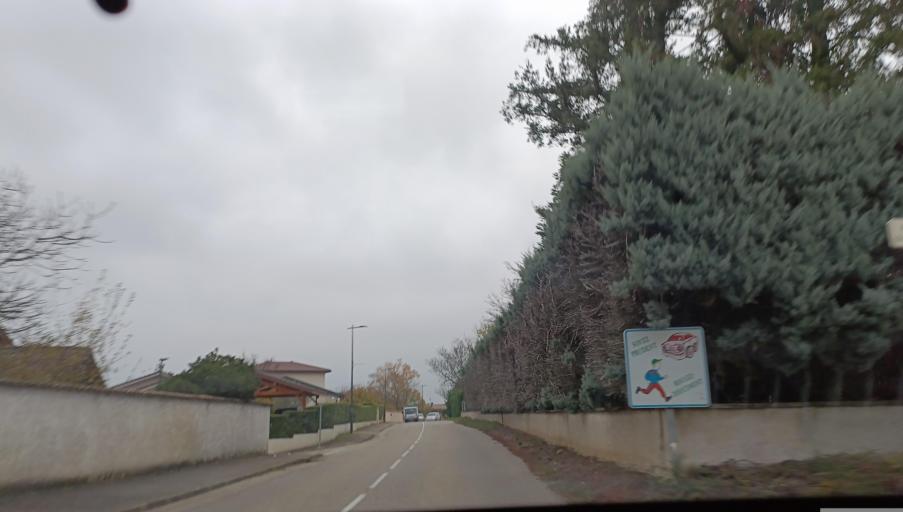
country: FR
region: Rhone-Alpes
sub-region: Departement de l'Isere
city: Serpaize
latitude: 45.5567
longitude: 4.9236
